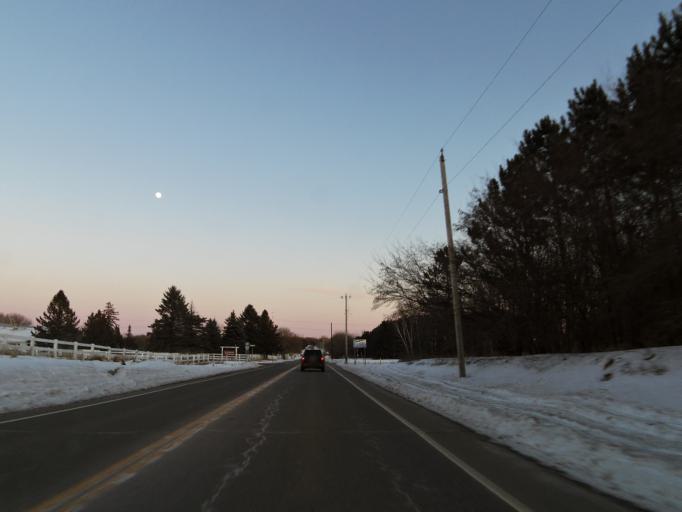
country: US
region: Minnesota
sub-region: Washington County
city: Grant
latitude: 45.0844
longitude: -92.9215
